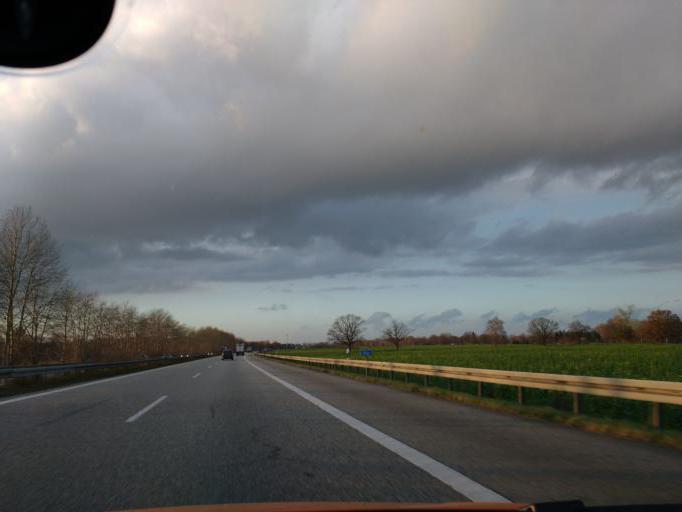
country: DE
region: Mecklenburg-Vorpommern
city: Neustadt-Glewe
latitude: 53.3963
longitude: 11.5885
